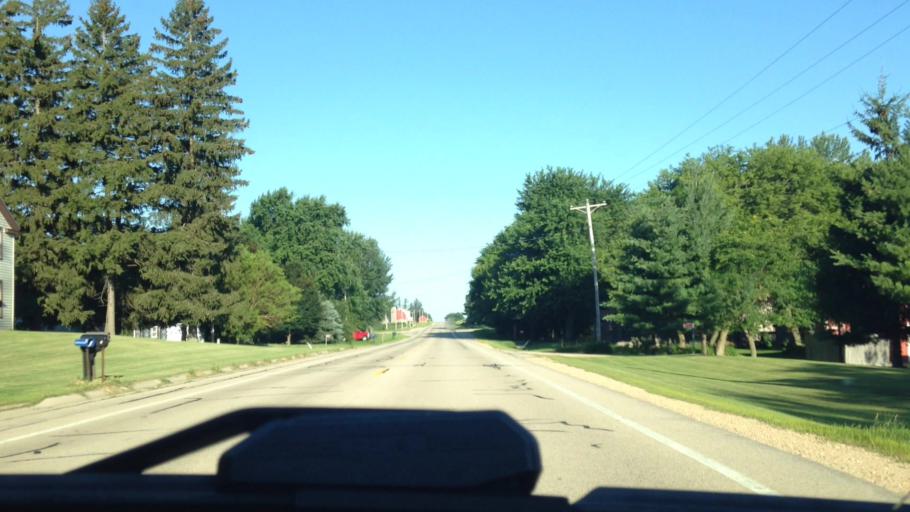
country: US
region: Wisconsin
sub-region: Dane County
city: De Forest
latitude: 43.3326
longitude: -89.2822
